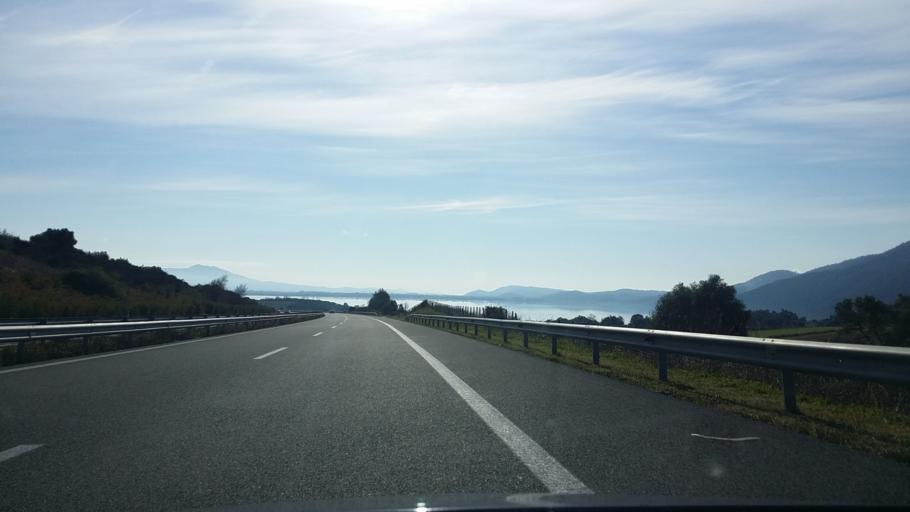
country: GR
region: West Greece
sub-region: Nomos Aitolias kai Akarnanias
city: Fitiai
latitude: 38.6855
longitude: 21.2165
